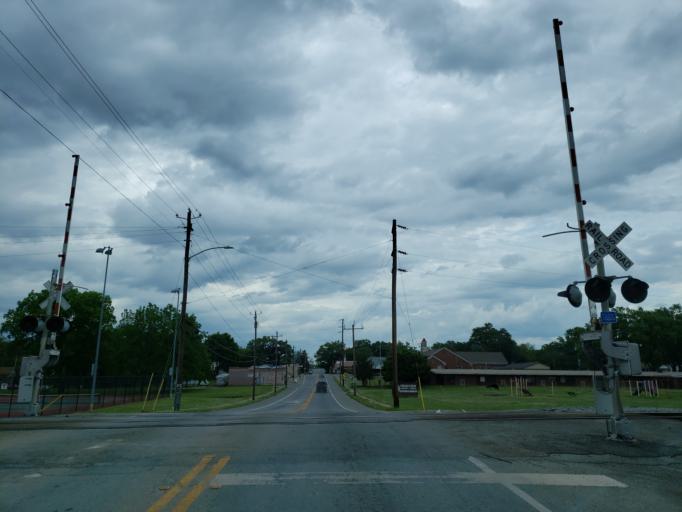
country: US
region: Georgia
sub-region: Polk County
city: Rockmart
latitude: 34.0002
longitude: -85.0414
